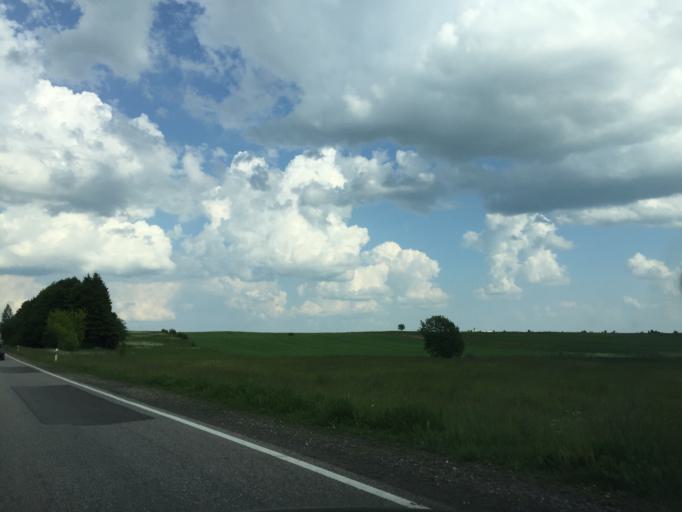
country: LT
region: Klaipedos apskritis
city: Kretinga
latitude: 55.8964
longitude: 21.1789
